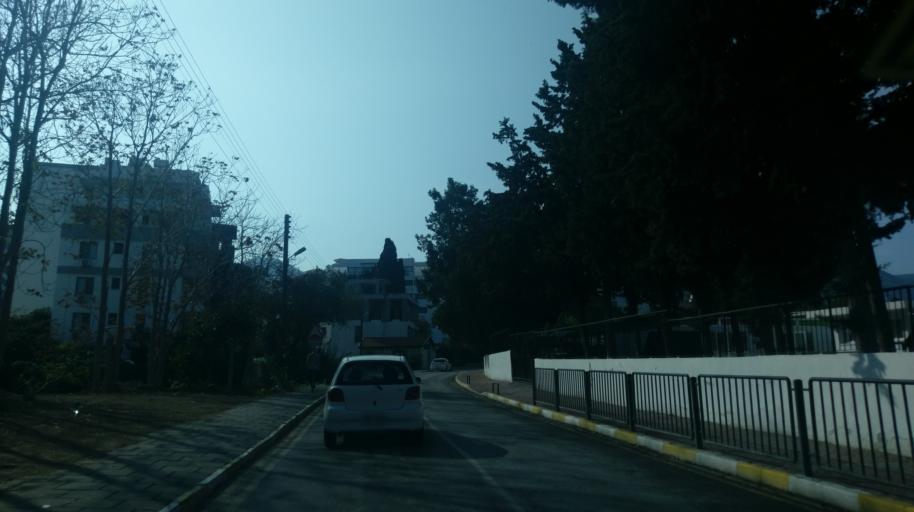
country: CY
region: Keryneia
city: Kyrenia
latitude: 35.3361
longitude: 33.3190
